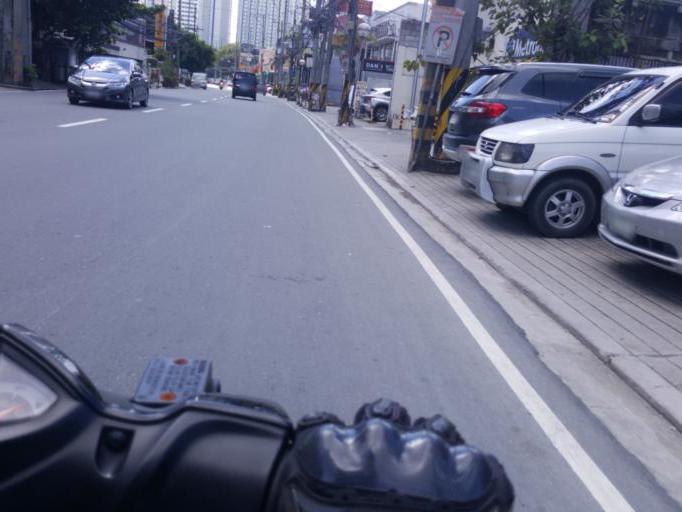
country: PH
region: Metro Manila
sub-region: Makati City
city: Makati City
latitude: 14.5624
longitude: 121.0272
